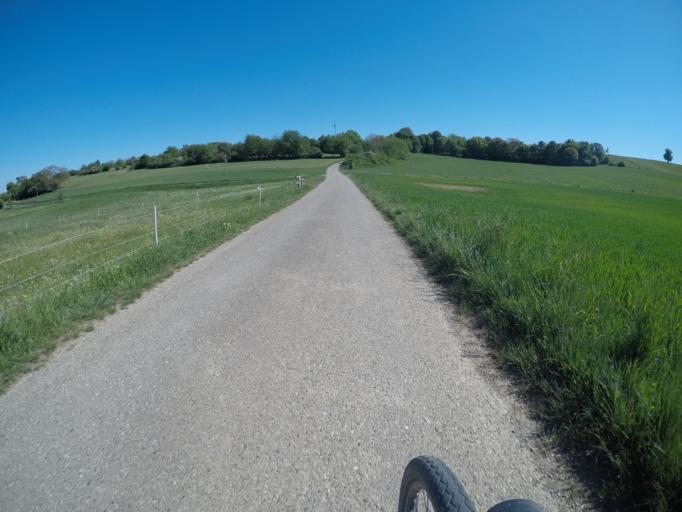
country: DE
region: Baden-Wuerttemberg
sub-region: Regierungsbezirk Stuttgart
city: Weissach
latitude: 48.8364
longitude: 8.8988
